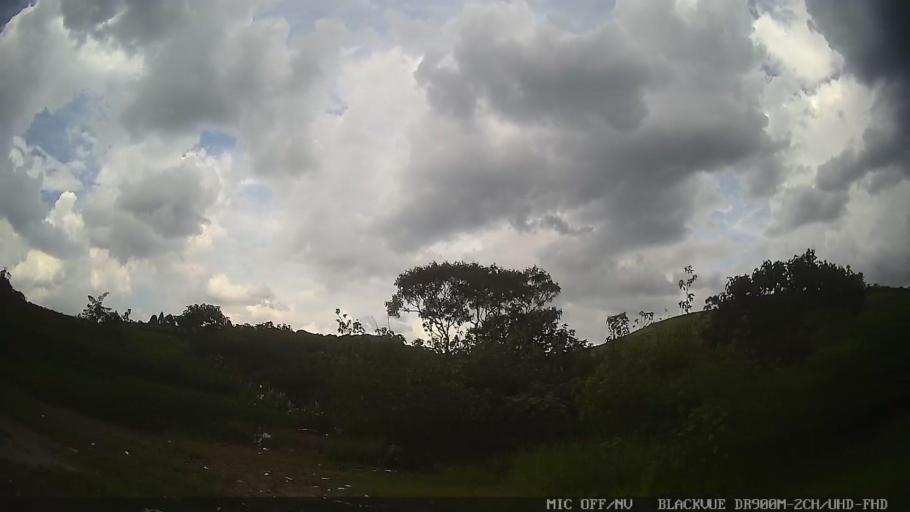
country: BR
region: Sao Paulo
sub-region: Ribeirao Pires
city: Ribeirao Pires
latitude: -23.6873
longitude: -46.4267
